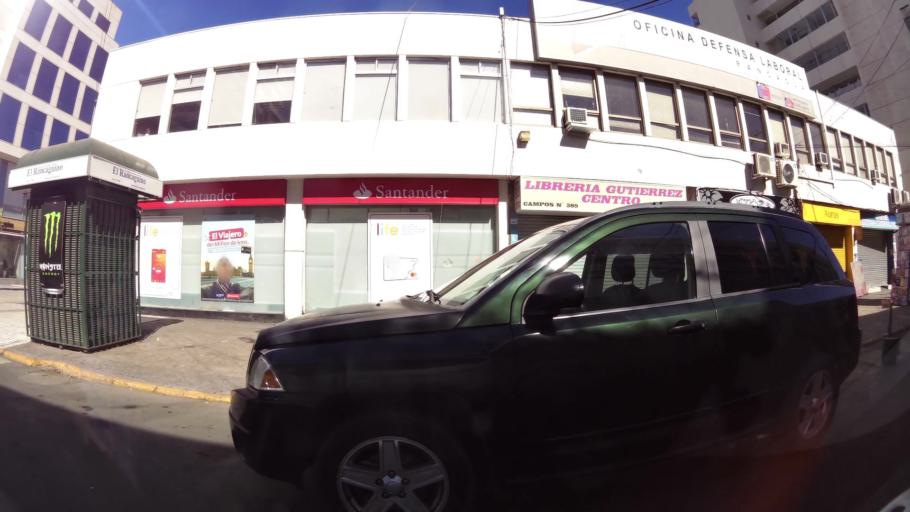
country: CL
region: O'Higgins
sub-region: Provincia de Cachapoal
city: Rancagua
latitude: -34.1700
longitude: -70.7422
